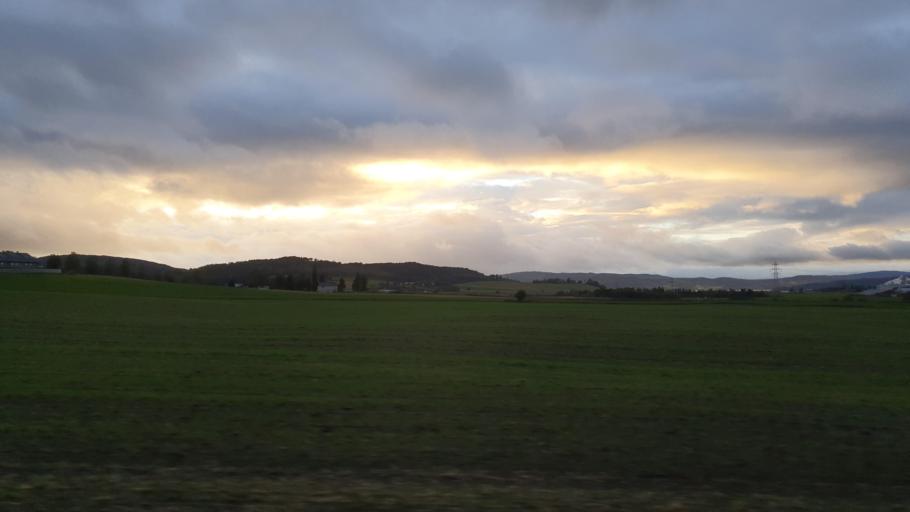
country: NO
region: Nord-Trondelag
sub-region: Levanger
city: Skogn
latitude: 63.6869
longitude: 11.1798
